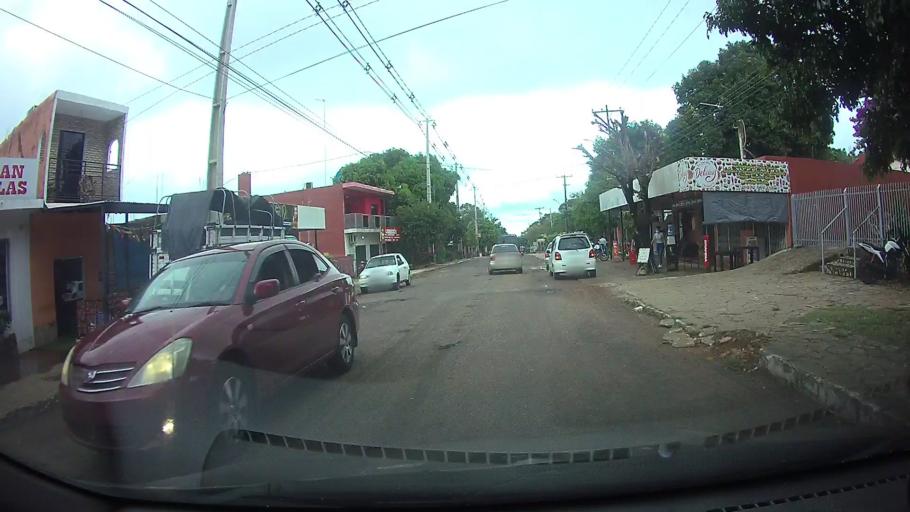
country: PY
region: Cordillera
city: Altos
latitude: -25.2655
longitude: -57.2499
